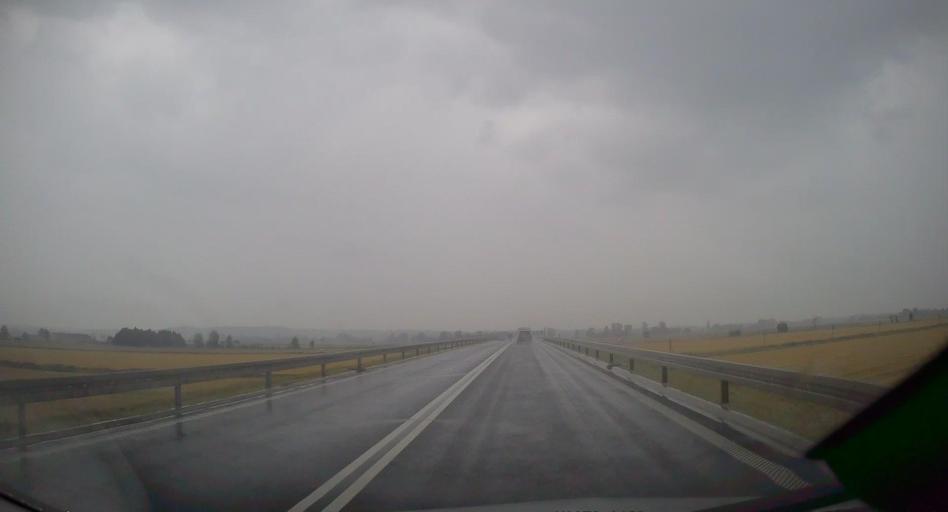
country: PL
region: Opole Voivodeship
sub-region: Powiat nyski
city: Nysa
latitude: 50.4663
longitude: 17.4061
